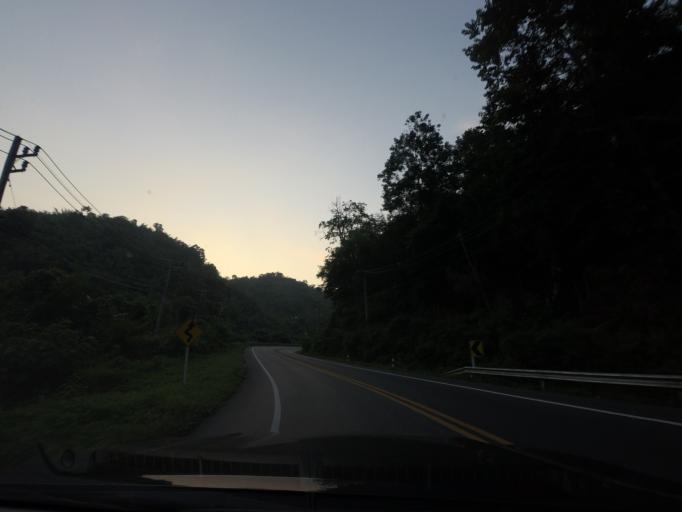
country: TH
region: Nan
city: Na Noi
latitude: 18.4265
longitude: 100.6960
